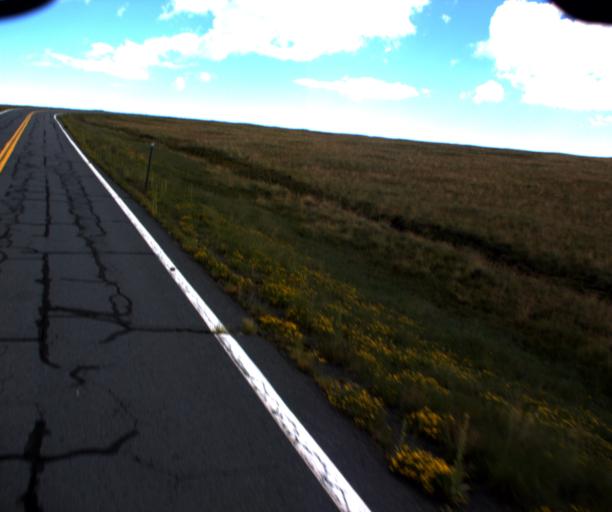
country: US
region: Arizona
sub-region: Apache County
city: Eagar
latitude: 33.9580
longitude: -109.3939
